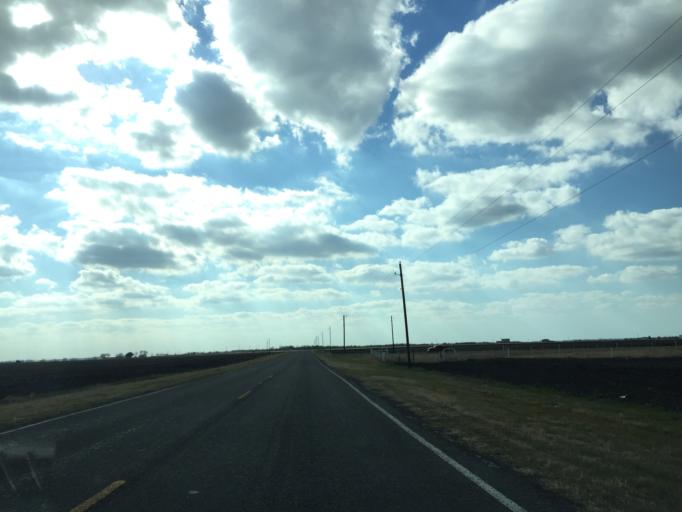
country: US
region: Texas
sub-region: Williamson County
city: Granger
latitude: 30.6753
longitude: -97.3448
